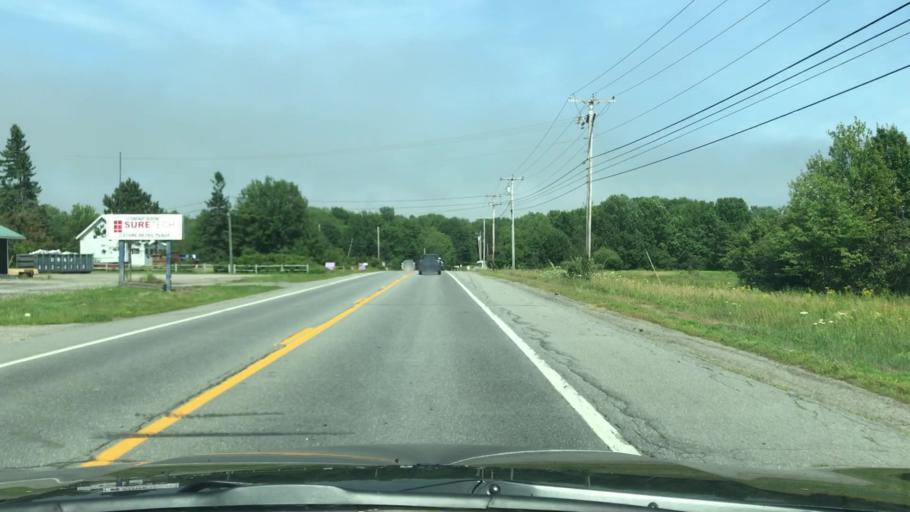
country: US
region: Maine
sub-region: Waldo County
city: Belfast
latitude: 44.4325
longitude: -68.9574
